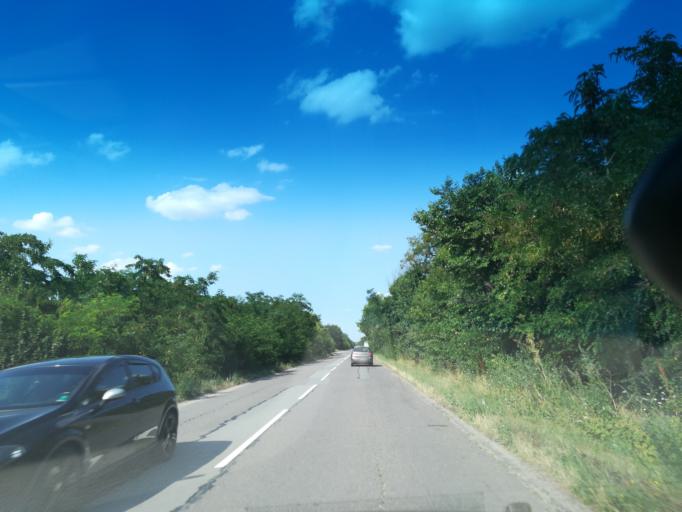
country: BG
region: Stara Zagora
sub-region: Obshtina Chirpan
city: Chirpan
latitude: 42.2399
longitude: 25.4020
